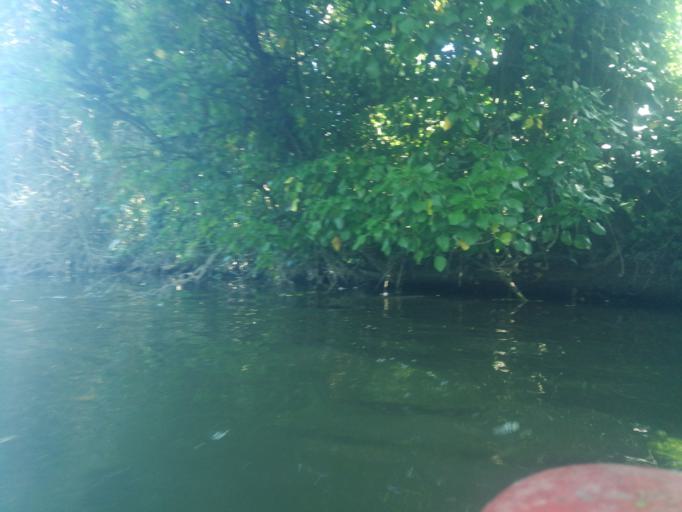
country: FR
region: Poitou-Charentes
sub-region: Departement de la Charente-Maritime
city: Marans
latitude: 46.3626
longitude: -0.9582
